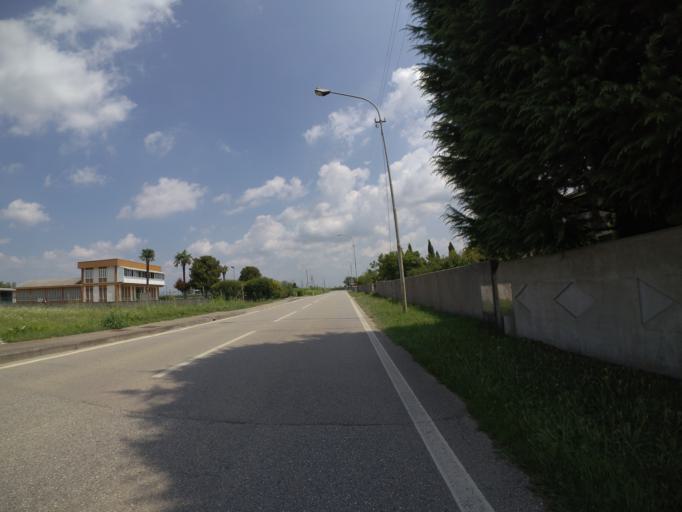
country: IT
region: Friuli Venezia Giulia
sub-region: Provincia di Udine
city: Mereto di Tomba
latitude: 46.0246
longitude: 13.0429
